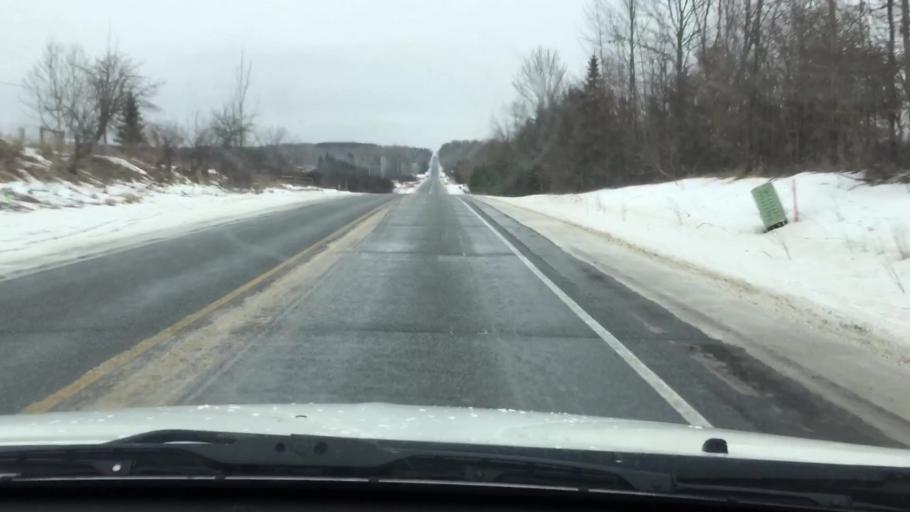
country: US
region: Michigan
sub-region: Wexford County
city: Cadillac
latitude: 44.1089
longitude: -85.4443
